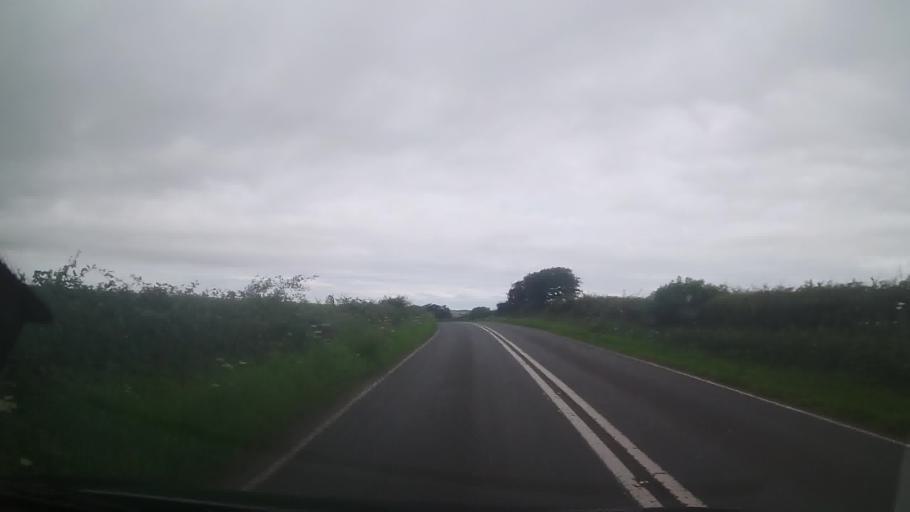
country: GB
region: Wales
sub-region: Gwynedd
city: Caernarfon
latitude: 53.1758
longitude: -4.2900
